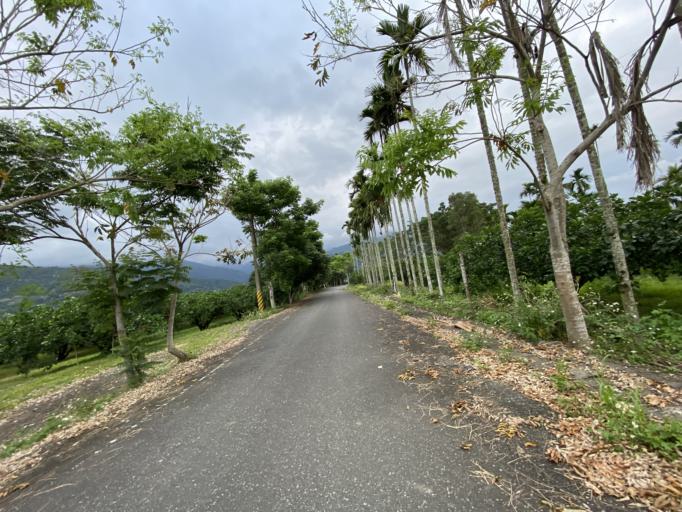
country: TW
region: Taiwan
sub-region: Hualien
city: Hualian
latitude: 23.4698
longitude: 121.3595
